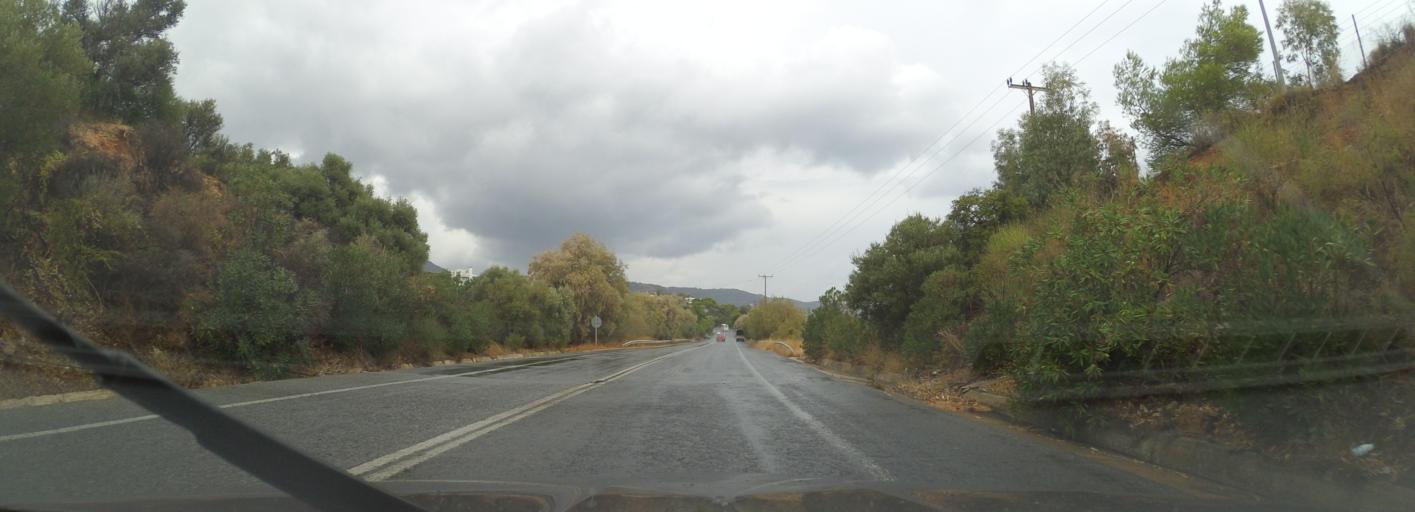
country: GR
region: Crete
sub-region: Nomos Irakleiou
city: Gazi
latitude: 35.3494
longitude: 25.0429
